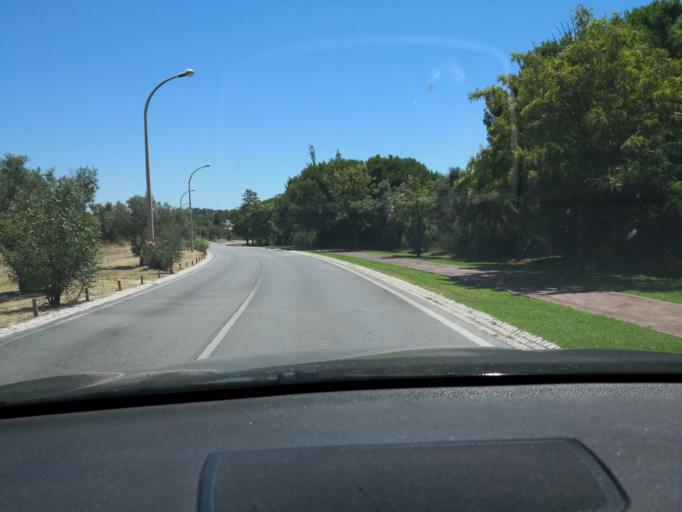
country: PT
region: Faro
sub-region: Loule
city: Vilamoura
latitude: 37.1041
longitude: -8.1279
